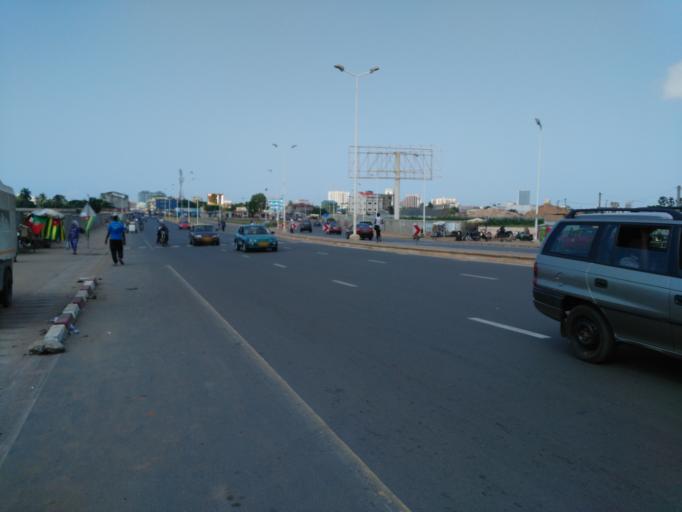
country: TG
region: Maritime
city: Lome
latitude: 6.1466
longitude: 1.2300
